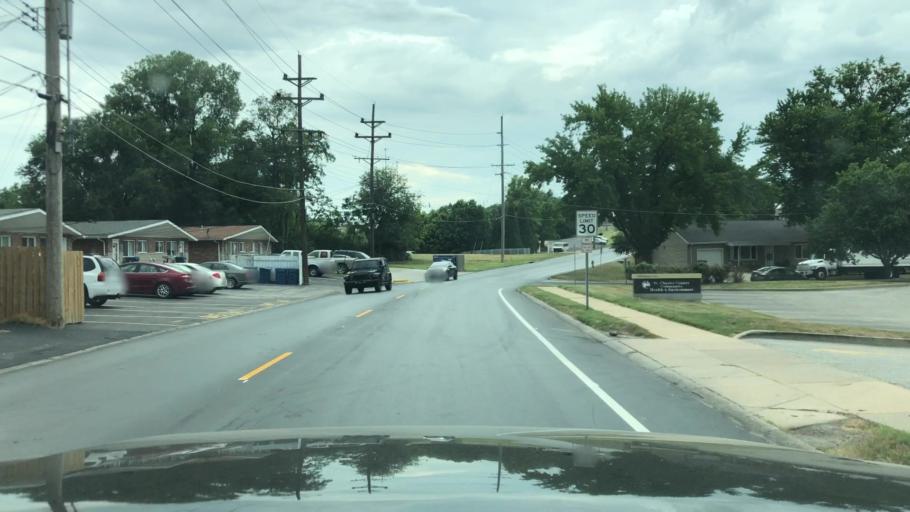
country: US
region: Missouri
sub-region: Saint Charles County
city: Saint Charles
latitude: 38.7748
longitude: -90.5070
